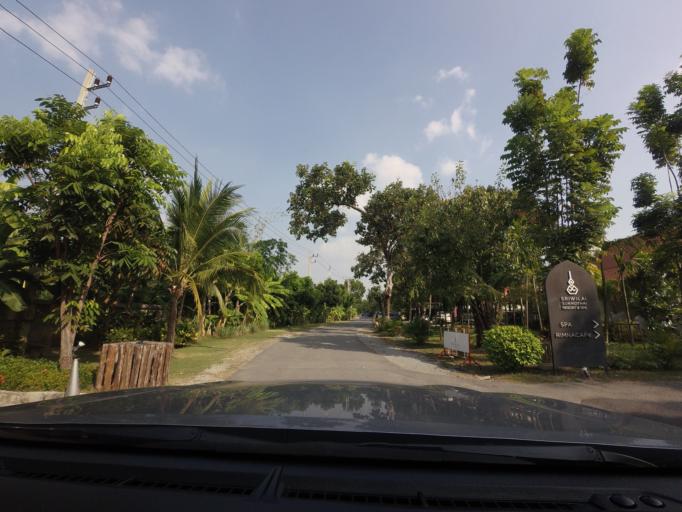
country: TH
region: Sukhothai
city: Ban Na
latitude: 17.0162
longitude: 99.7243
